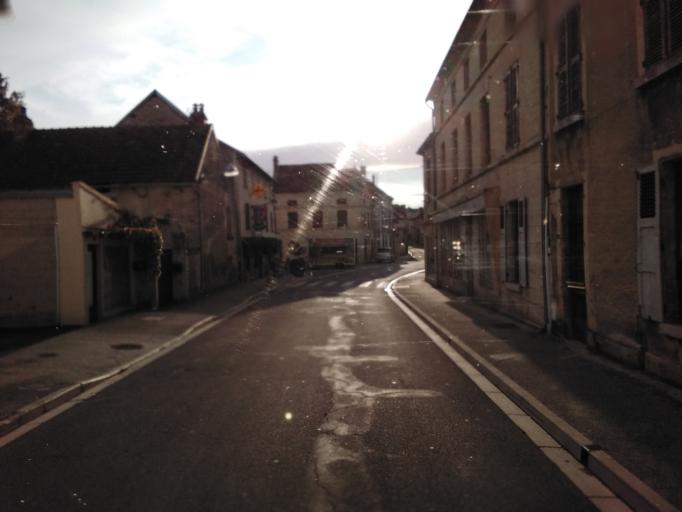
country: FR
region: Champagne-Ardenne
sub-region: Departement de l'Aube
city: Les Riceys
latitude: 47.8426
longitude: 4.3652
